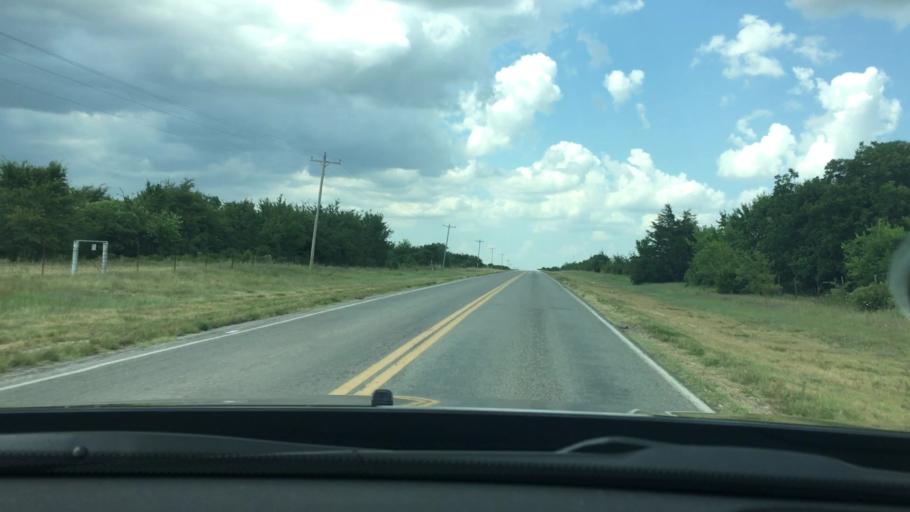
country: US
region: Oklahoma
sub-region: Pontotoc County
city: Ada
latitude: 34.5360
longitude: -96.6346
